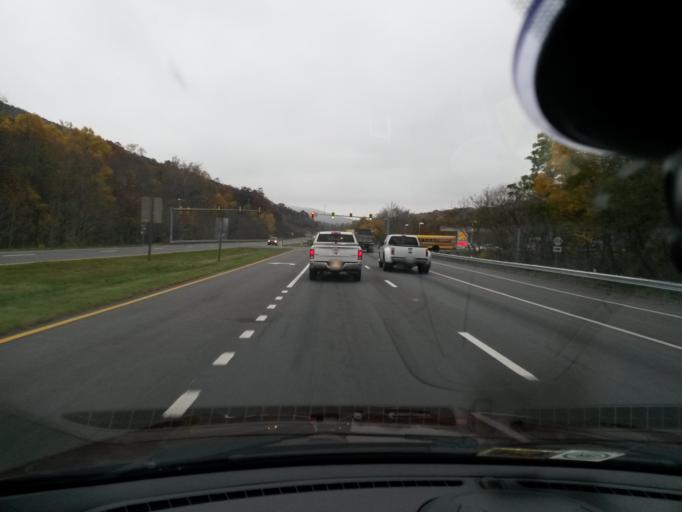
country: US
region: Virginia
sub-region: Botetourt County
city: Cloverdale
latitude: 37.3535
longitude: -79.8842
